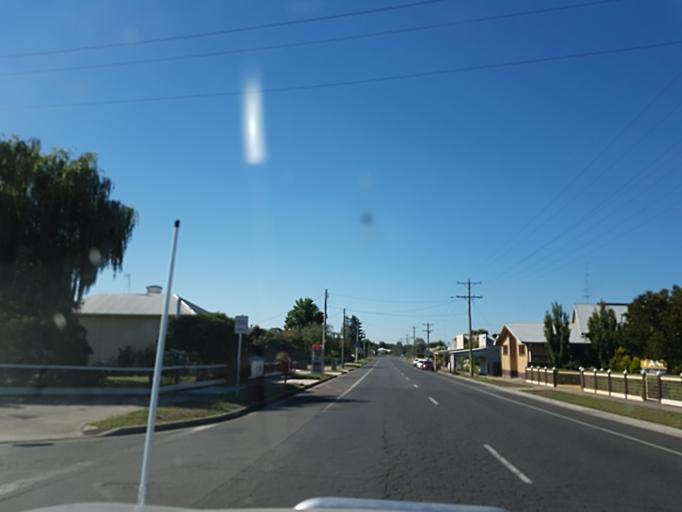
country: AU
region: Victoria
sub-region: Colac-Otway
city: Colac
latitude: -38.3606
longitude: 143.5830
